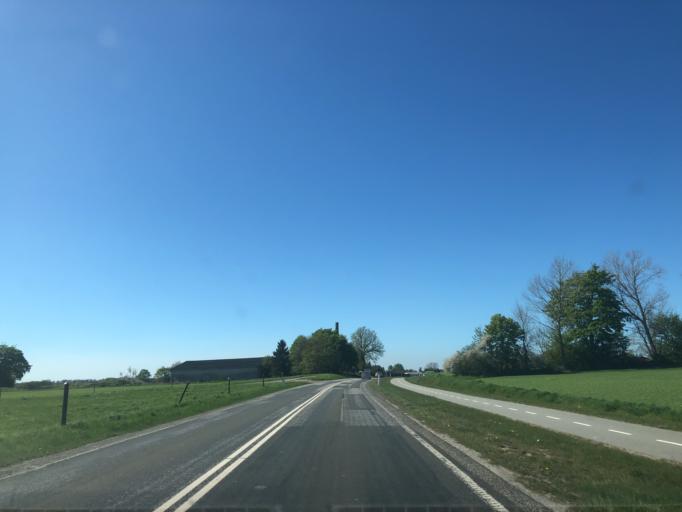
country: DK
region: Zealand
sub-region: Stevns Kommune
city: Stroby Egede
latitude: 55.3734
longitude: 12.2965
